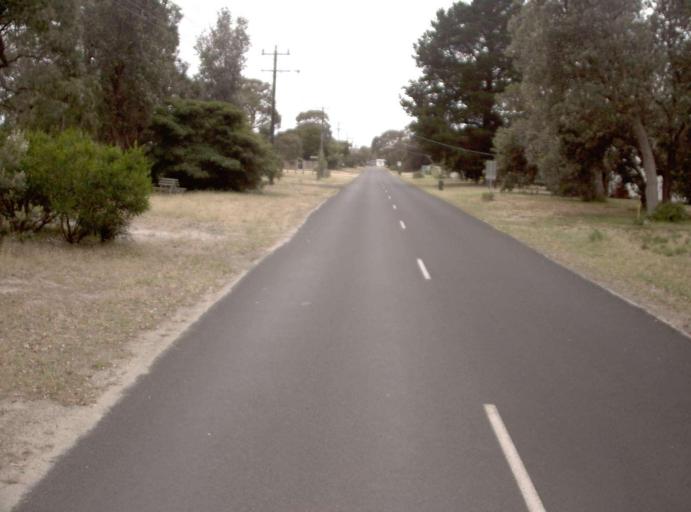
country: AU
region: Victoria
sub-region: East Gippsland
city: Bairnsdale
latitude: -38.0567
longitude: 147.5697
